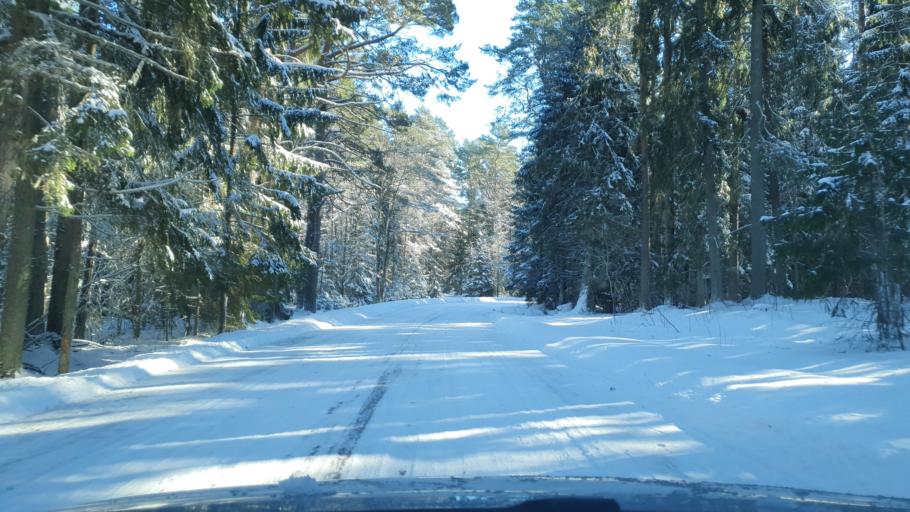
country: EE
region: Laeaene-Virumaa
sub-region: Haljala vald
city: Haljala
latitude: 59.6015
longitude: 26.0770
